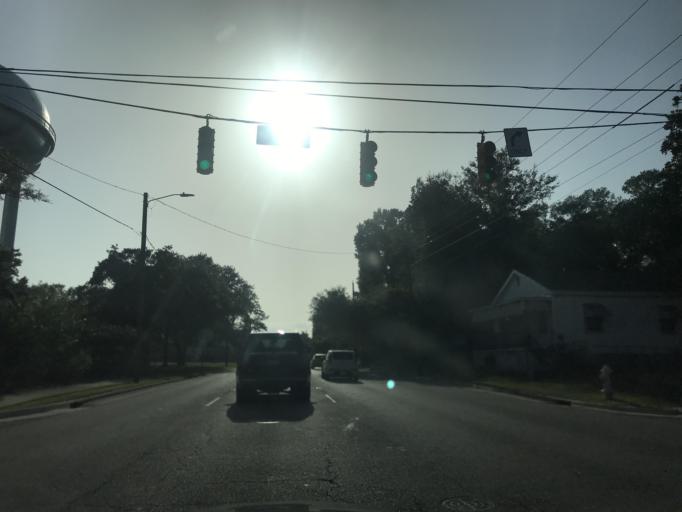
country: US
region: North Carolina
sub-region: New Hanover County
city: Wilmington
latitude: 34.2262
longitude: -77.9355
